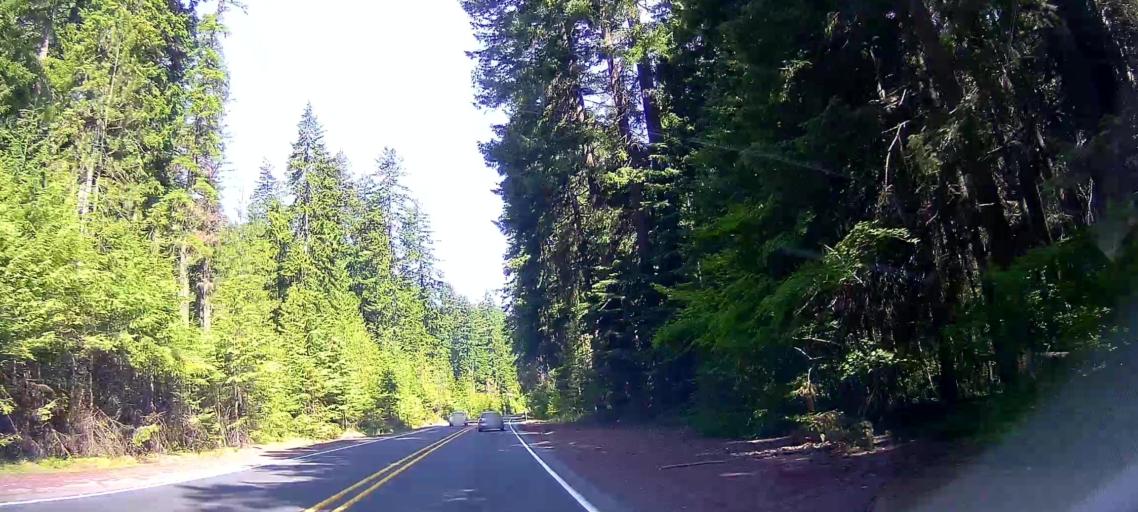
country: US
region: Oregon
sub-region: Jefferson County
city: Warm Springs
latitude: 45.1099
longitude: -121.5634
